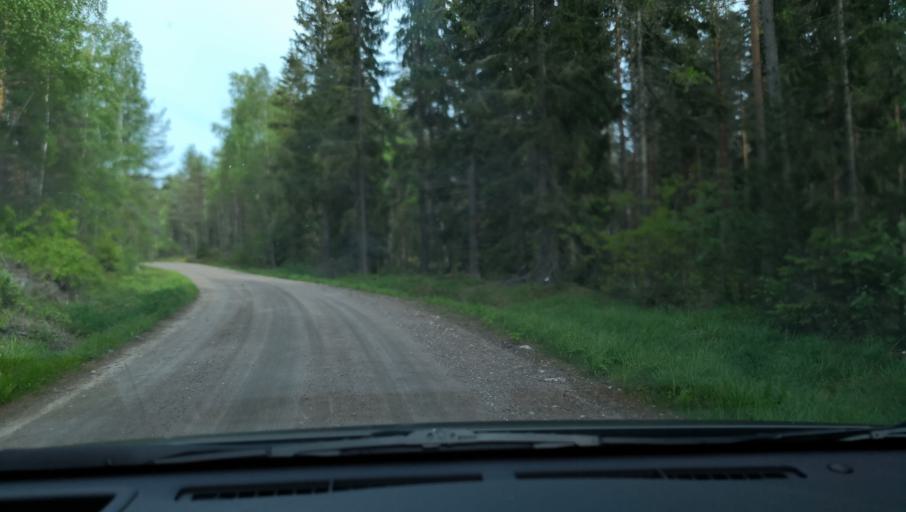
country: SE
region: Vaestmanland
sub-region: Arboga Kommun
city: Tyringe
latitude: 59.3631
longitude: 15.9750
